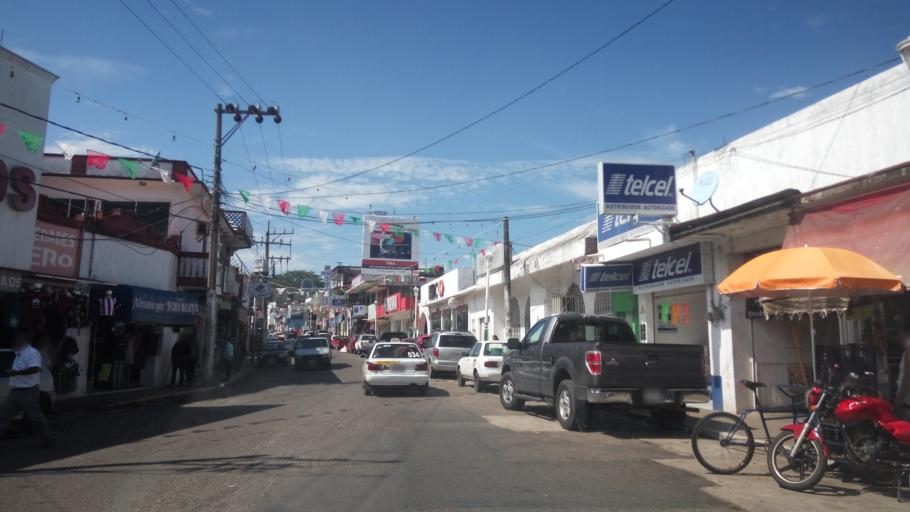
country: MX
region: Tabasco
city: Teapa
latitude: 17.5511
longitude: -92.9522
